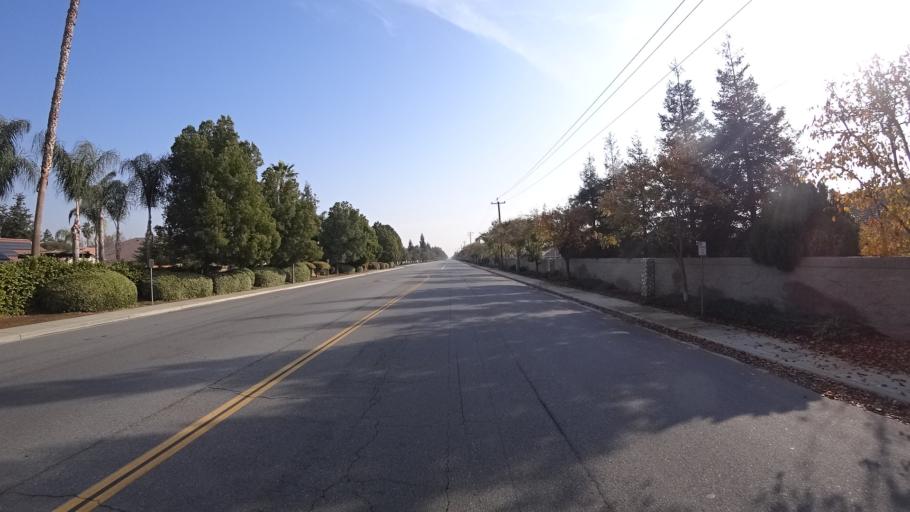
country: US
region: California
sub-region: Kern County
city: Greenacres
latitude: 35.4197
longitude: -119.1025
